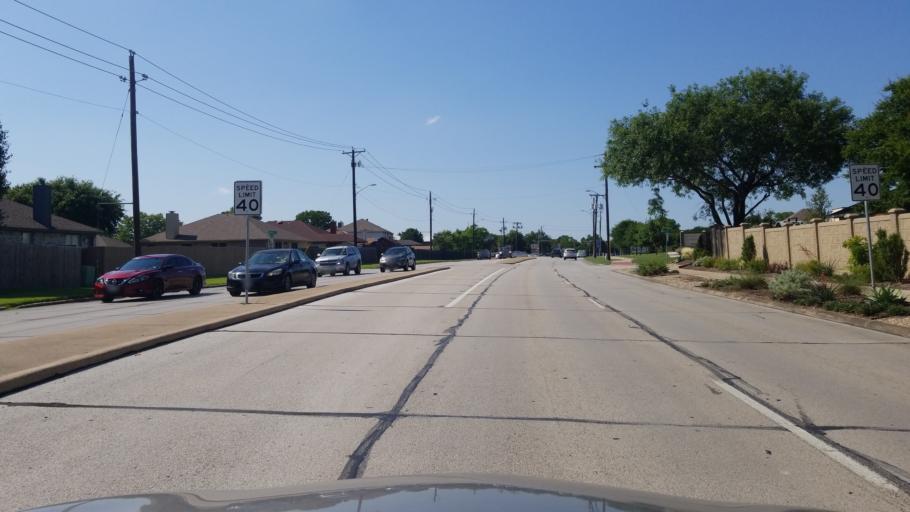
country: US
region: Texas
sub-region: Dallas County
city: Grand Prairie
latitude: 32.6898
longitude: -97.0153
